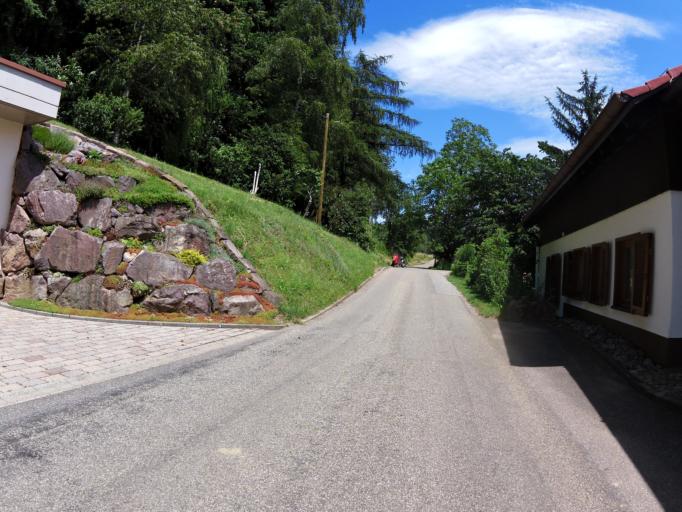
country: DE
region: Baden-Wuerttemberg
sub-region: Freiburg Region
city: Seelbach
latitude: 48.3305
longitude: 7.9830
